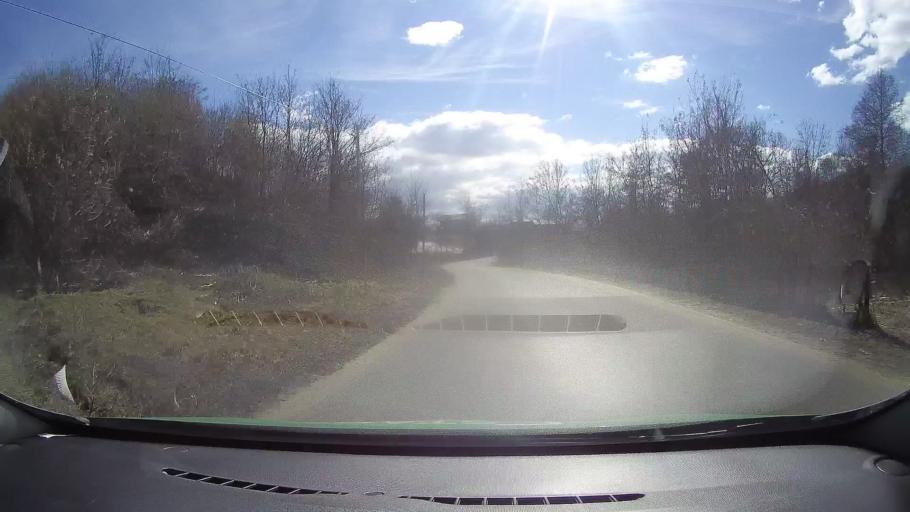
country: RO
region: Dambovita
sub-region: Comuna Vulcana-Pandele
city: Gura Vulcanei
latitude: 45.0396
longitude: 25.3909
